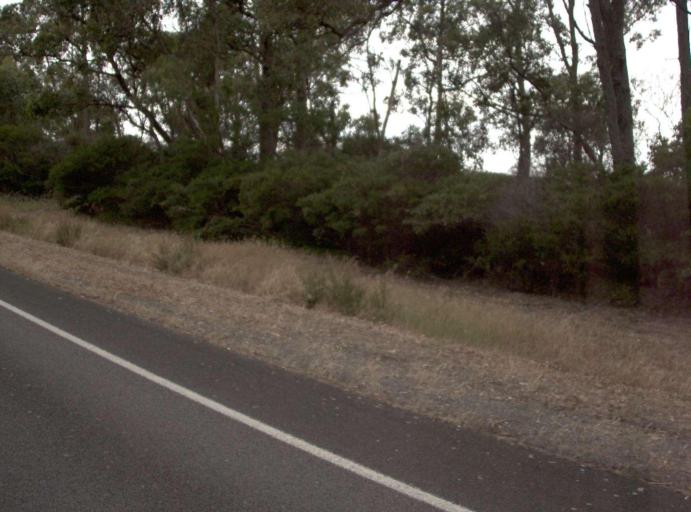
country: AU
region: Victoria
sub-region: Wellington
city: Sale
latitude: -38.4822
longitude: 146.9179
